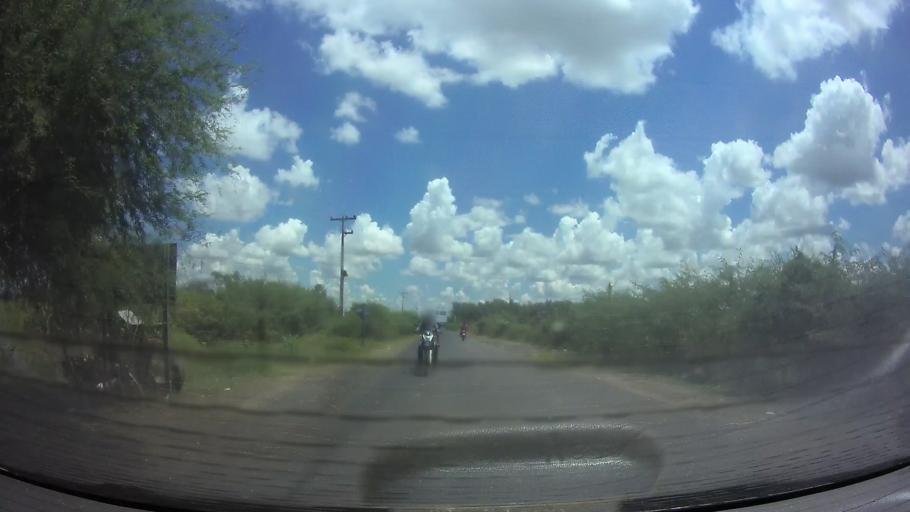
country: PY
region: Presidente Hayes
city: Nanawa
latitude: -25.2448
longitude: -57.6659
